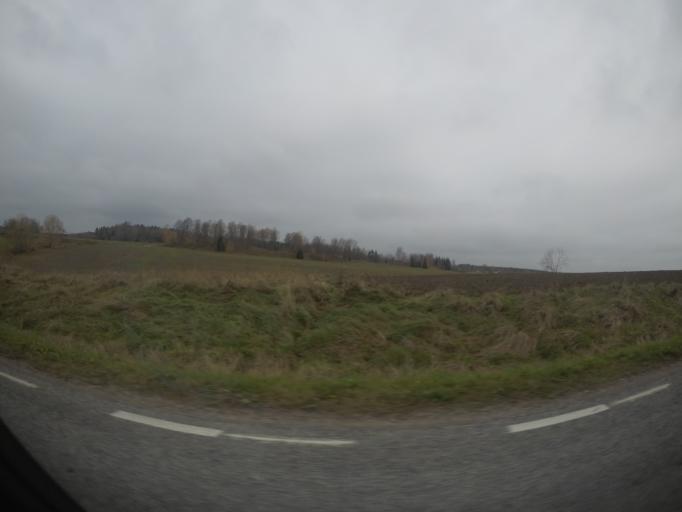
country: SE
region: Vaestmanland
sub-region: Vasteras
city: Skultuna
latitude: 59.6905
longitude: 16.4254
